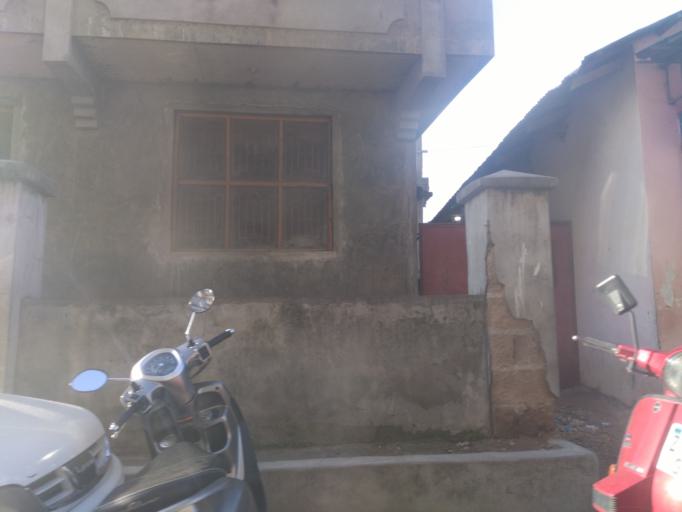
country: TZ
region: Zanzibar Urban/West
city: Zanzibar
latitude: -6.1652
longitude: 39.1958
